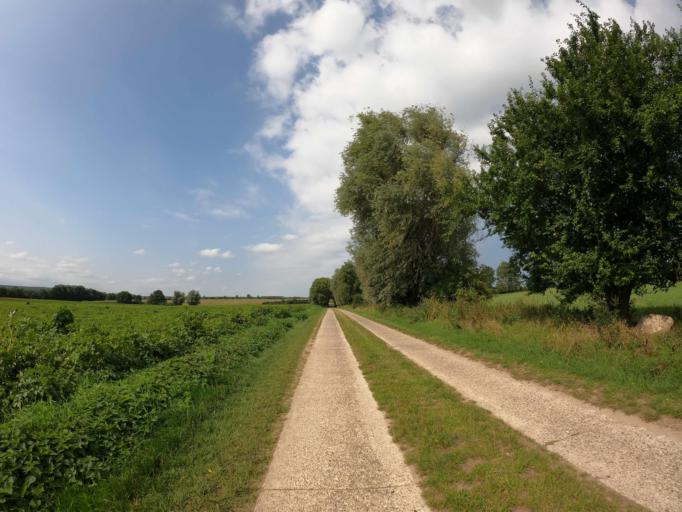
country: DE
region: Mecklenburg-Vorpommern
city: Malchow
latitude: 53.4391
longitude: 12.4831
